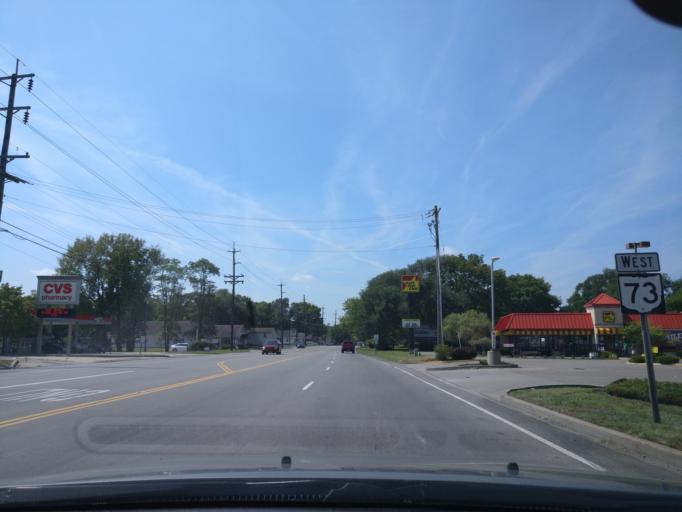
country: US
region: Ohio
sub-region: Butler County
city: Trenton
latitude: 39.4811
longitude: -84.4203
